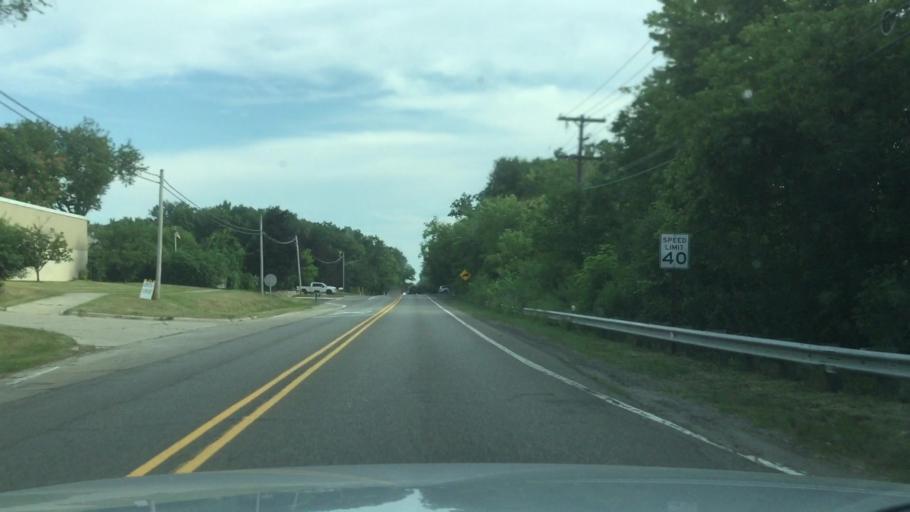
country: US
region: Michigan
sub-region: Oakland County
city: Sylvan Lake
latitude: 42.6725
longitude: -83.3474
